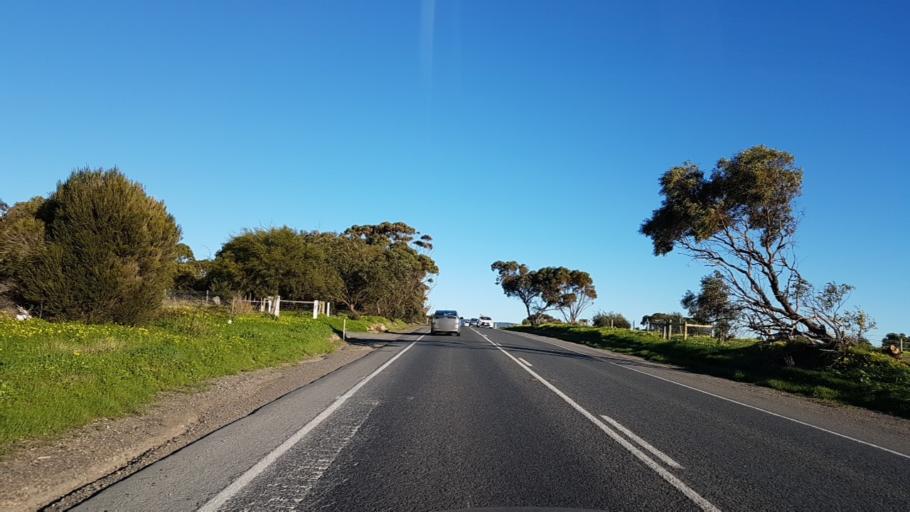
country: AU
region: South Australia
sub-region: Onkaparinga
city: Aldinga
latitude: -35.2479
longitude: 138.4945
